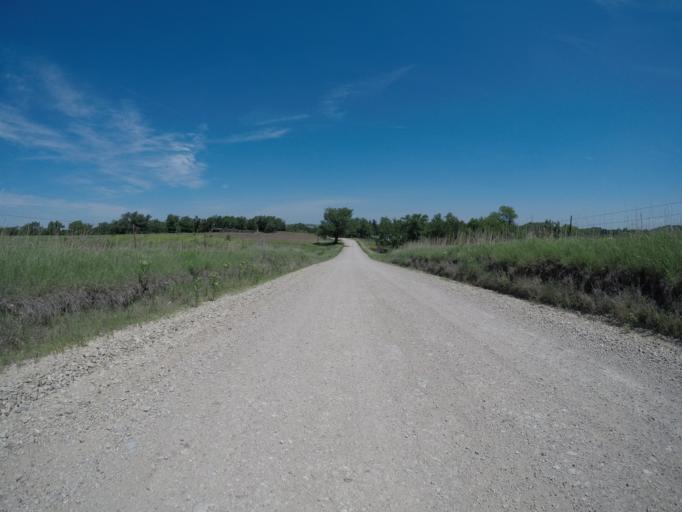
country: US
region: Kansas
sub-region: Wabaunsee County
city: Alma
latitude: 39.0482
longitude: -96.2151
